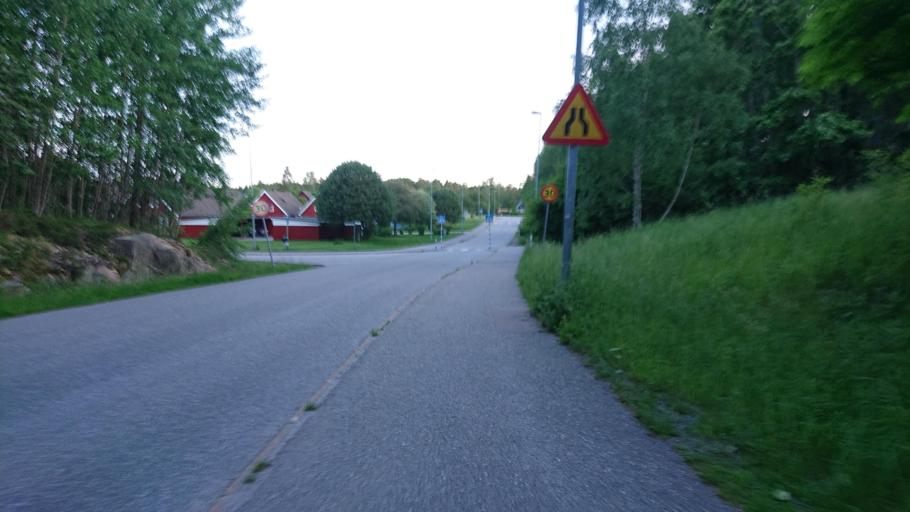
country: SE
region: Stockholm
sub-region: Osterakers Kommun
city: Akersberga
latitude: 59.4974
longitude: 18.3145
